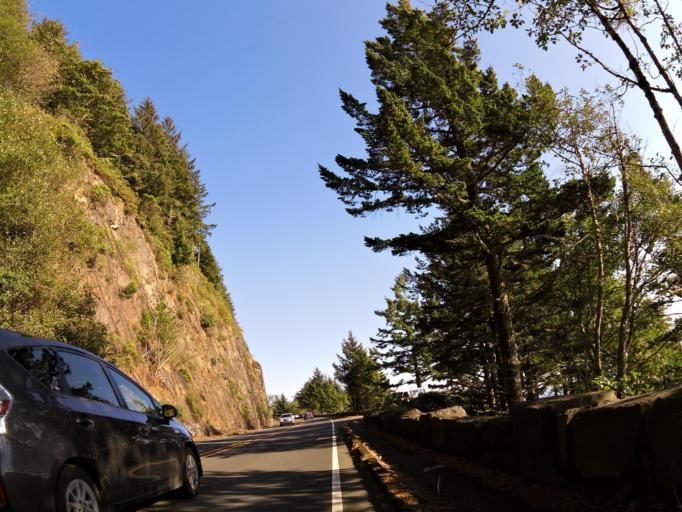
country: US
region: Oregon
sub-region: Tillamook County
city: Rockaway Beach
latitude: 45.7428
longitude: -123.9564
